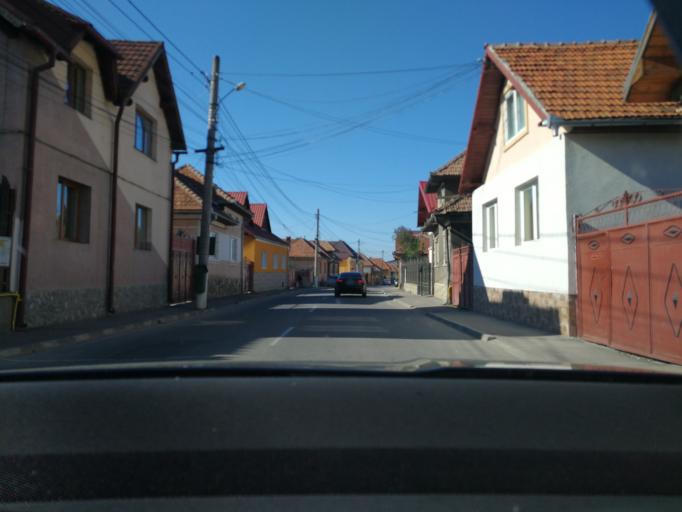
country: RO
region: Brasov
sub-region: Oras Rasnov
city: Rasnov
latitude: 45.5864
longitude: 25.4587
